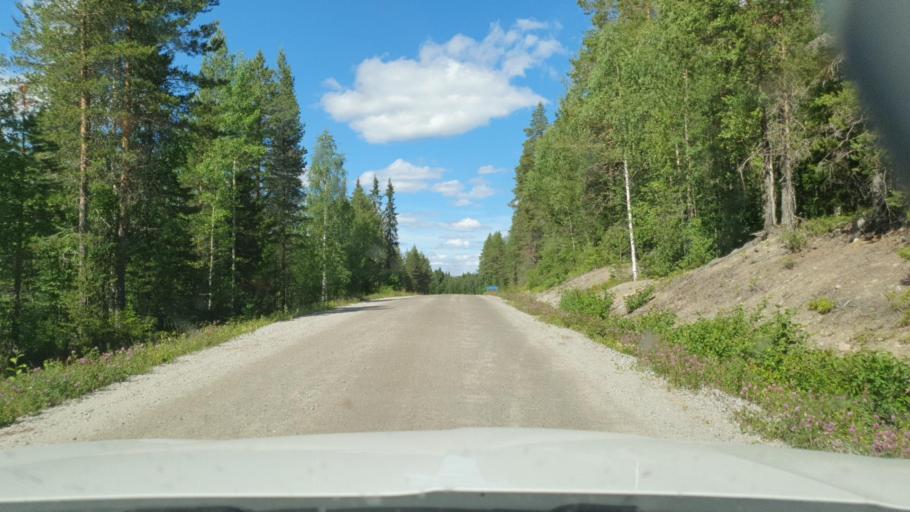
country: SE
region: Vaesterbotten
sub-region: Skelleftea Kommun
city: Backa
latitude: 65.1446
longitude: 21.1711
